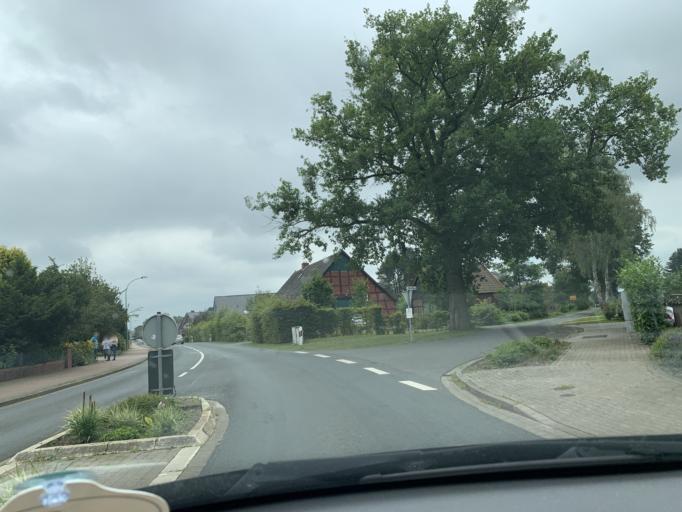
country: DE
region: North Rhine-Westphalia
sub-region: Regierungsbezirk Munster
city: Ostbevern
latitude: 52.1123
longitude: 7.8527
